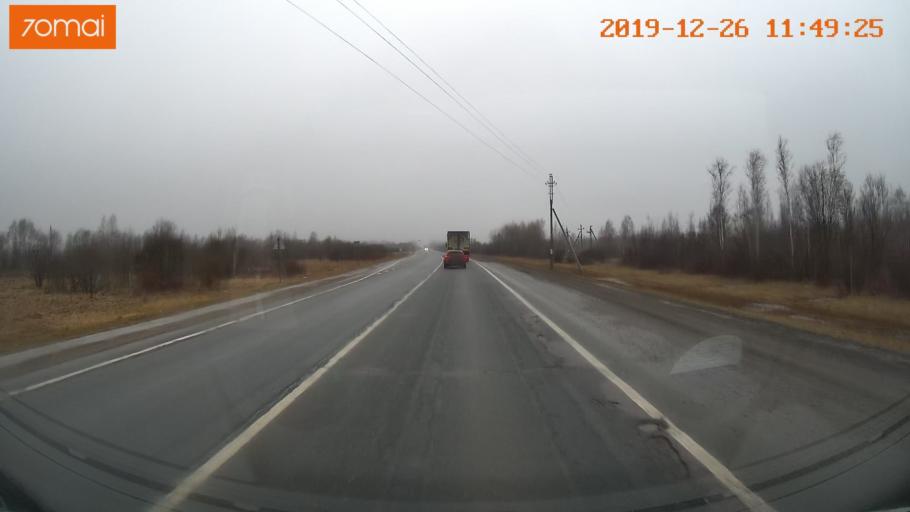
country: RU
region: Vologda
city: Sheksna
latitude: 59.2484
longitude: 38.4199
